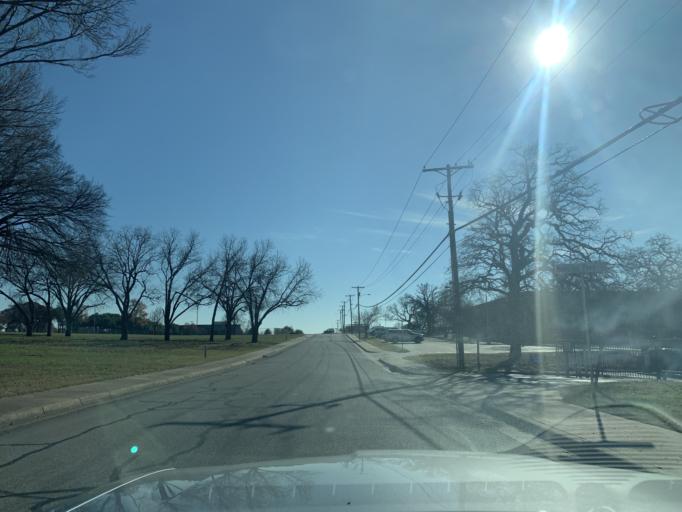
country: US
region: Texas
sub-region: Tarrant County
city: Bedford
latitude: 32.8432
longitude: -97.1402
